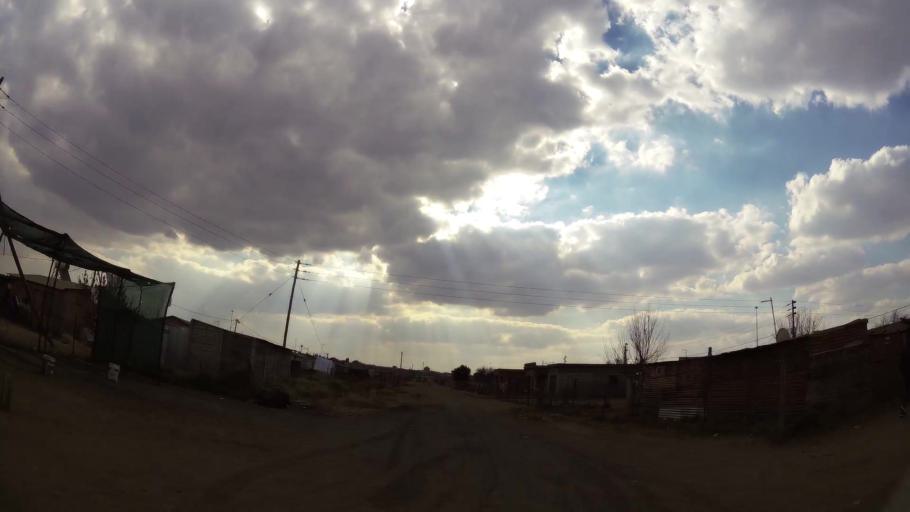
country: ZA
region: Mpumalanga
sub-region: Nkangala District Municipality
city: Delmas
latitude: -26.1412
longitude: 28.6929
